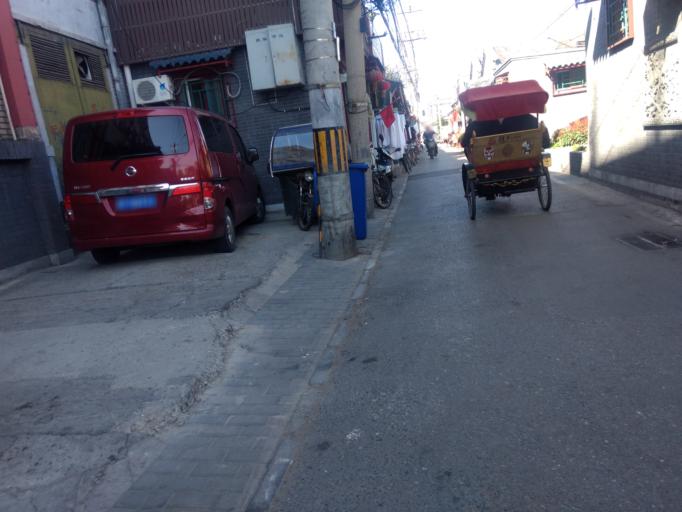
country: CN
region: Beijing
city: Beijing
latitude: 39.8906
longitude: 116.3836
